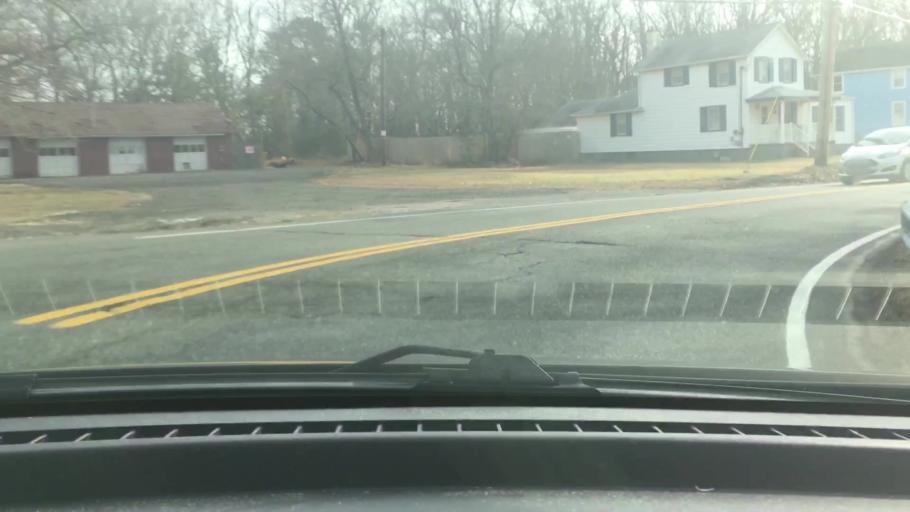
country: US
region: New Jersey
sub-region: Monmouth County
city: Shark River Hills
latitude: 40.2220
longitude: -74.0573
